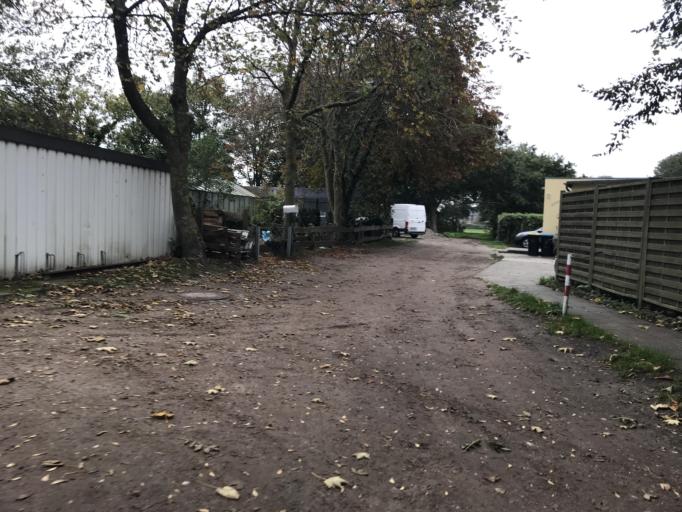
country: DE
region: Lower Saxony
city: Borkum
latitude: 53.5896
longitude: 6.6661
